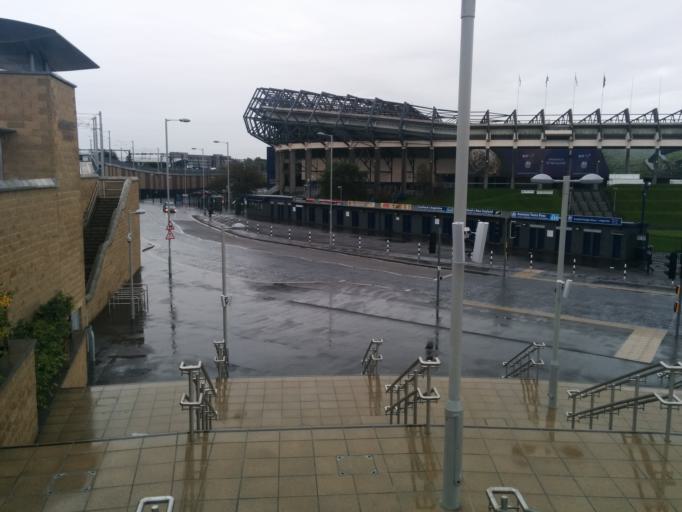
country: GB
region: Scotland
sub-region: Edinburgh
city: Colinton
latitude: 55.9422
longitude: -3.2373
